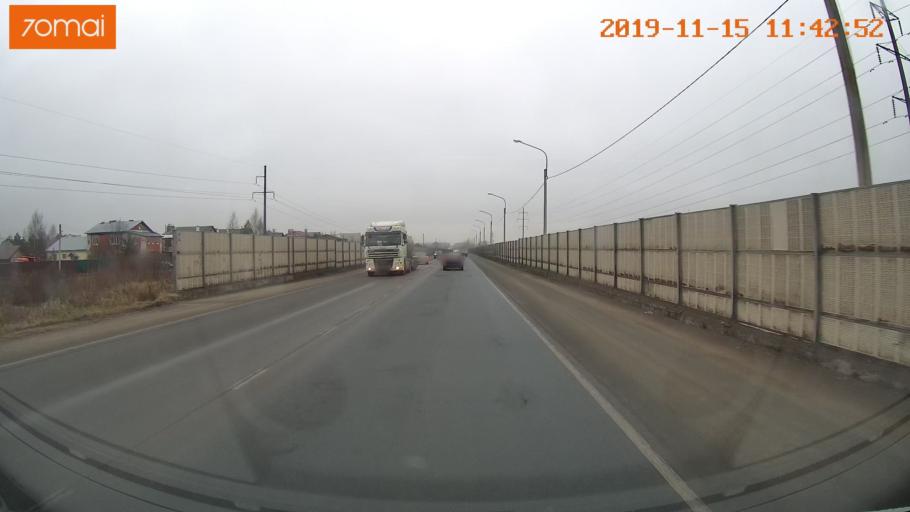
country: RU
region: Vologda
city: Vologda
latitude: 59.2229
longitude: 39.7747
